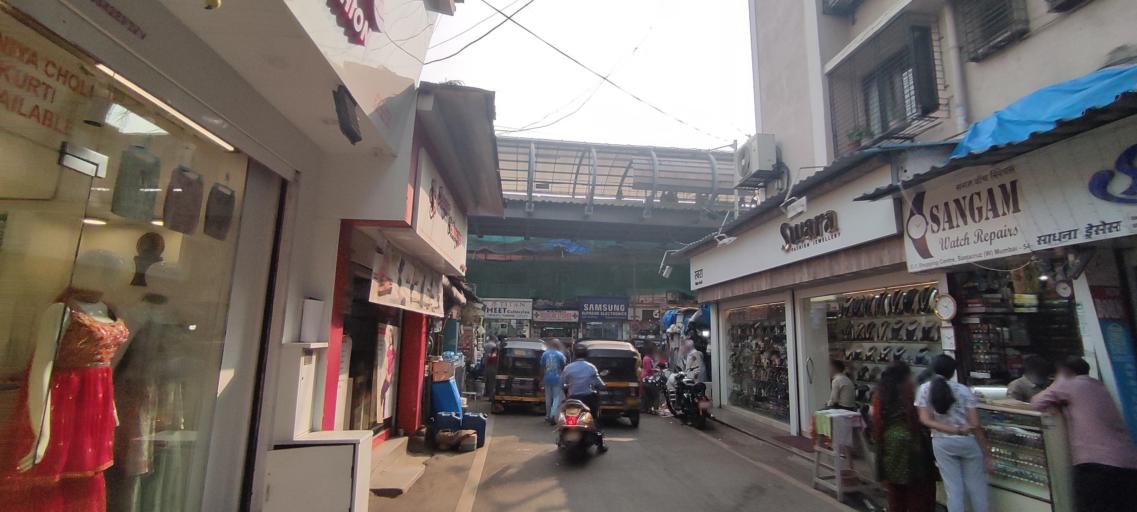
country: IN
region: Maharashtra
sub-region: Mumbai Suburban
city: Mumbai
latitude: 19.0810
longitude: 72.8409
